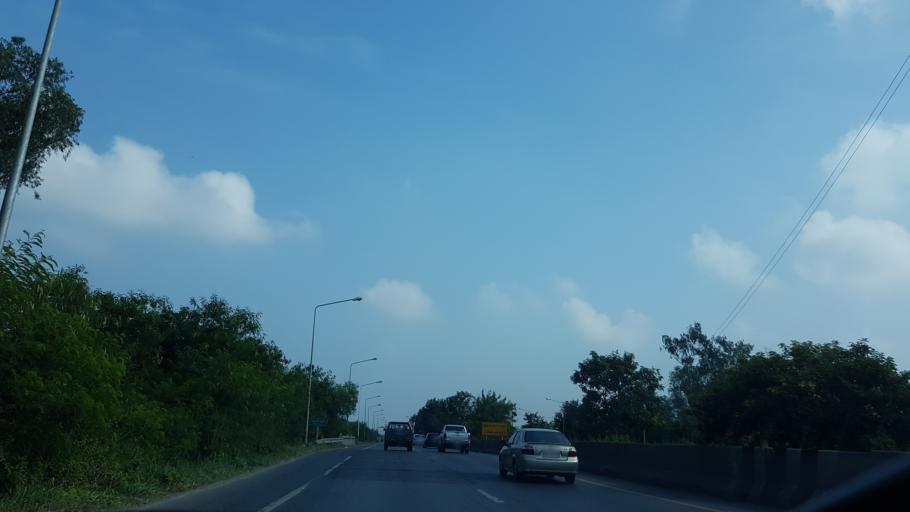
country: TH
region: Pathum Thani
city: Sam Khok
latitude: 14.1317
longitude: 100.5389
